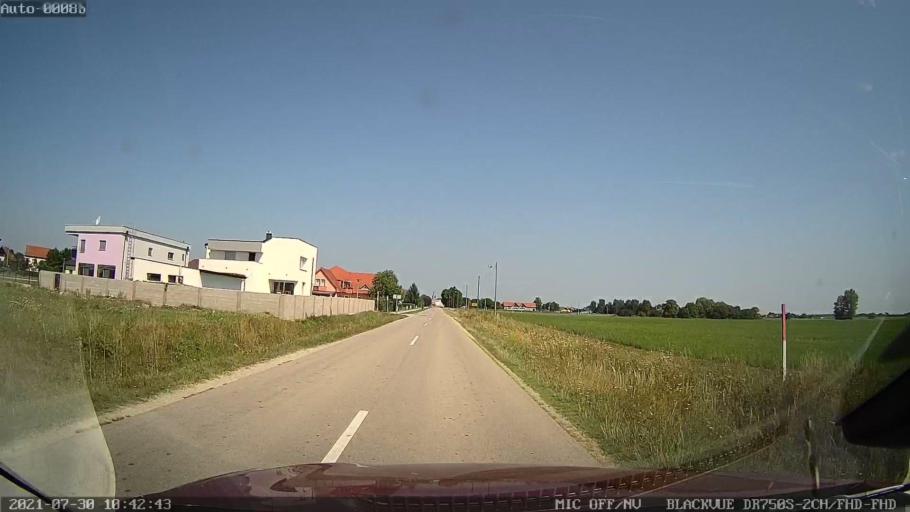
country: HR
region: Medimurska
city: Kursanec
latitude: 46.2874
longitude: 16.4080
